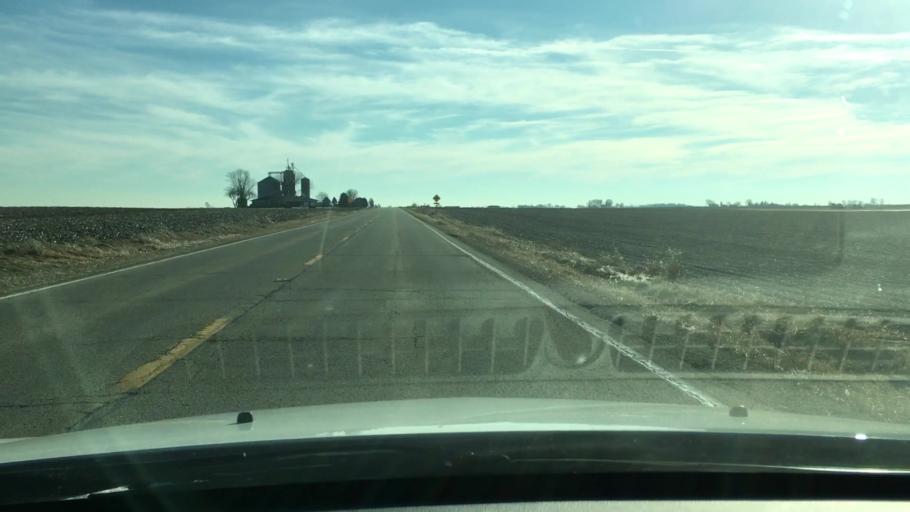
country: US
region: Illinois
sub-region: LaSalle County
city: Mendota
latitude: 41.5013
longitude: -89.1269
